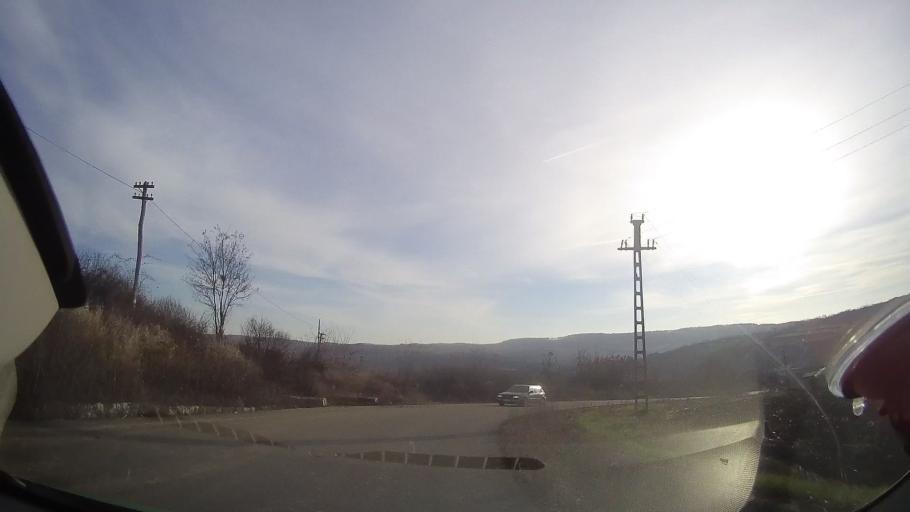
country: RO
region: Bihor
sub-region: Comuna Sarbi
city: Burzuc
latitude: 47.1596
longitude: 22.1637
